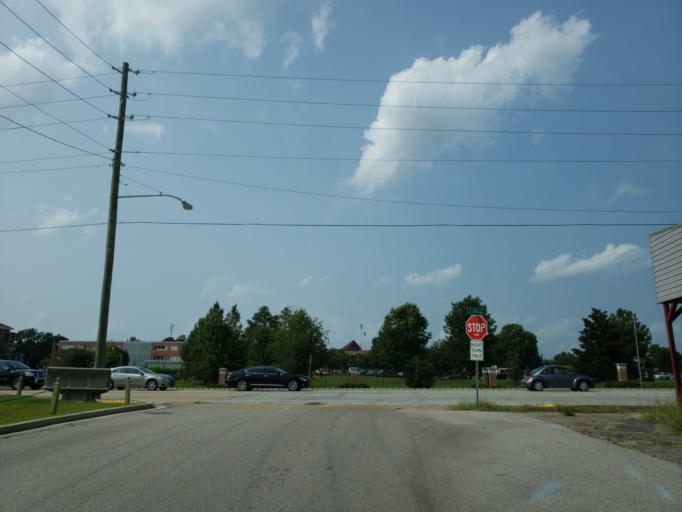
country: US
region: Mississippi
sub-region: Forrest County
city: Hattiesburg
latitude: 31.3244
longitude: -89.3301
